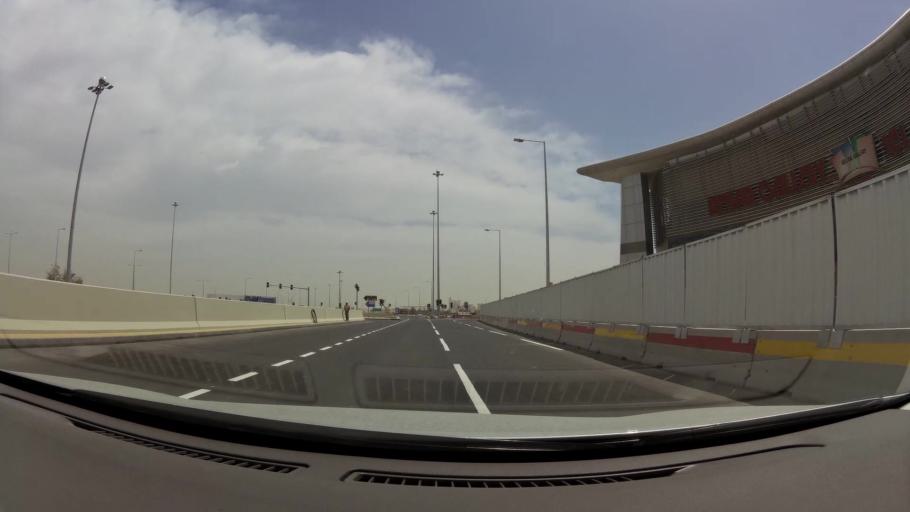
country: QA
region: Baladiyat ar Rayyan
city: Ar Rayyan
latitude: 25.3024
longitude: 51.4206
